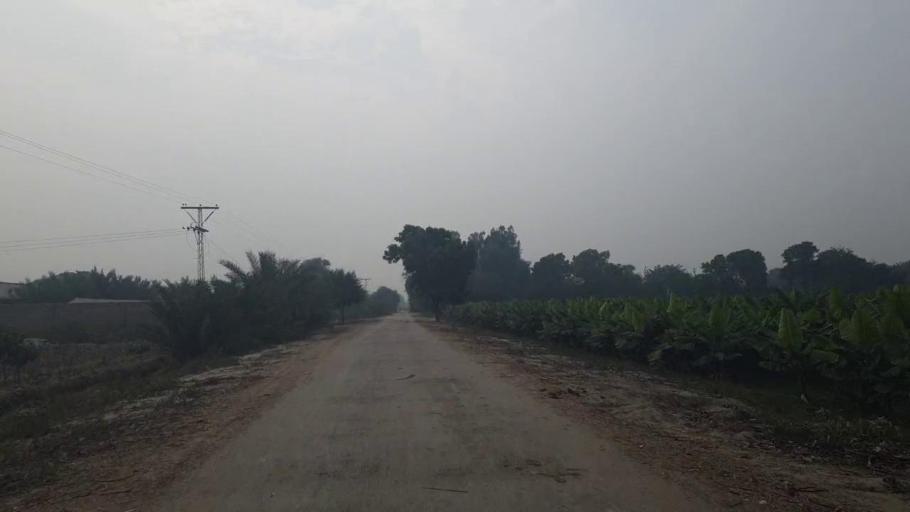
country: PK
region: Sindh
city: Tando Adam
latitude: 25.7210
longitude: 68.6803
